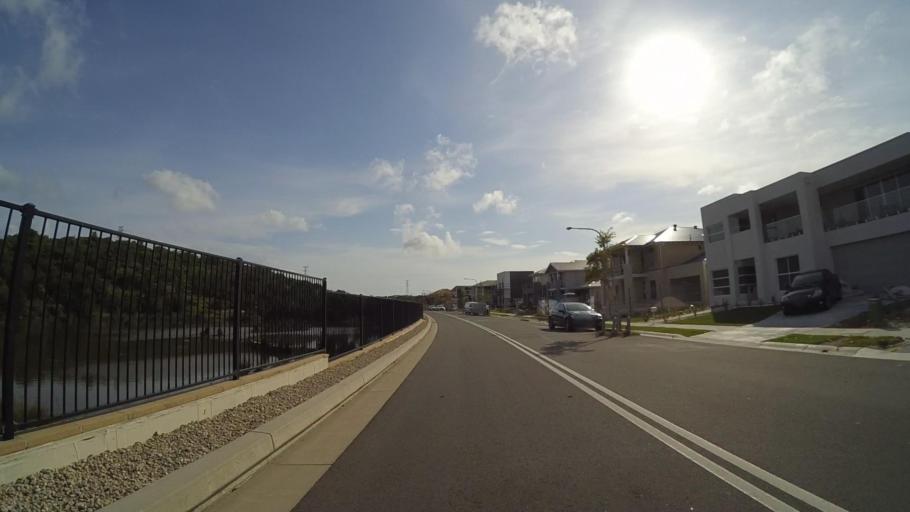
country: AU
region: New South Wales
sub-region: Sutherland Shire
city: Cronulla
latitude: -34.0334
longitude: 151.1669
